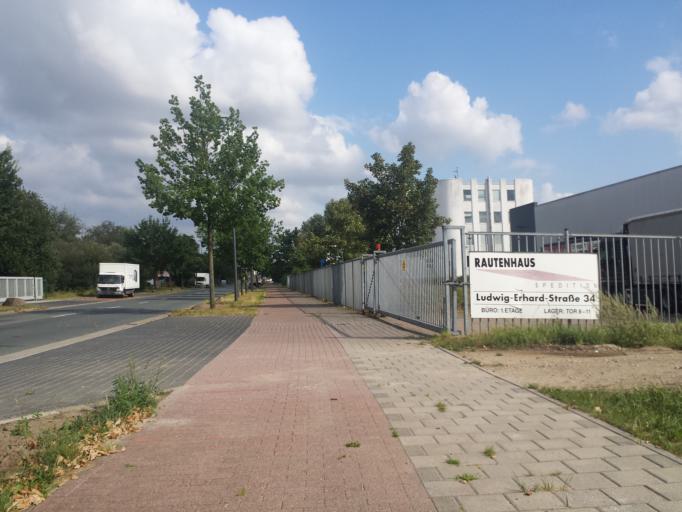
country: DE
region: Lower Saxony
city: Stuhr
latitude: 53.0918
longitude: 8.6998
